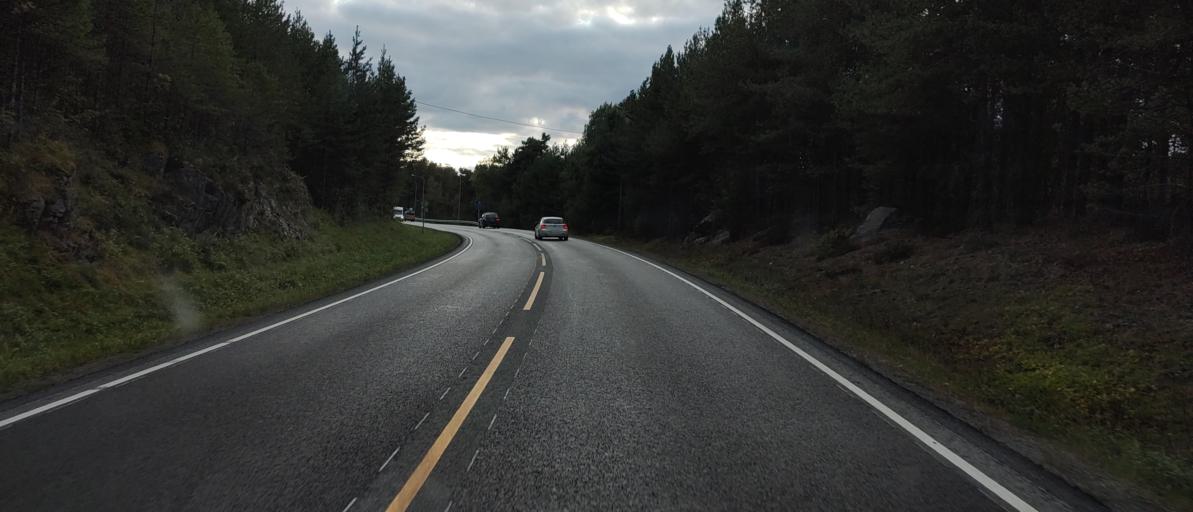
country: NO
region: More og Romsdal
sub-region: Molde
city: Molde
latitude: 62.7356
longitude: 7.2994
